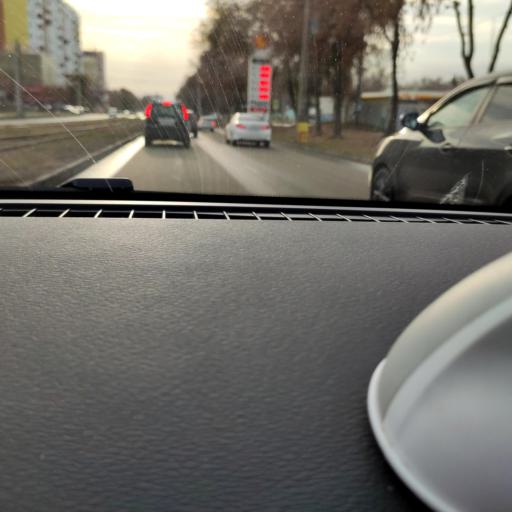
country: RU
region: Samara
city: Samara
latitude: 53.2296
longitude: 50.2275
